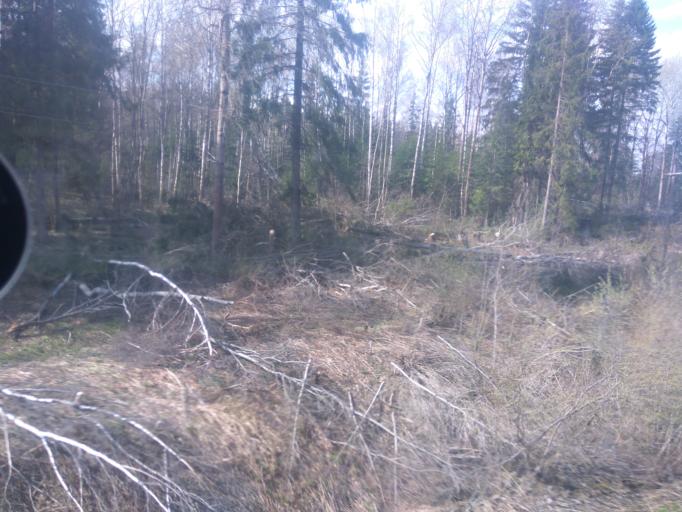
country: RU
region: Moskovskaya
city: Budenovetc
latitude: 56.2965
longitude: 37.6243
